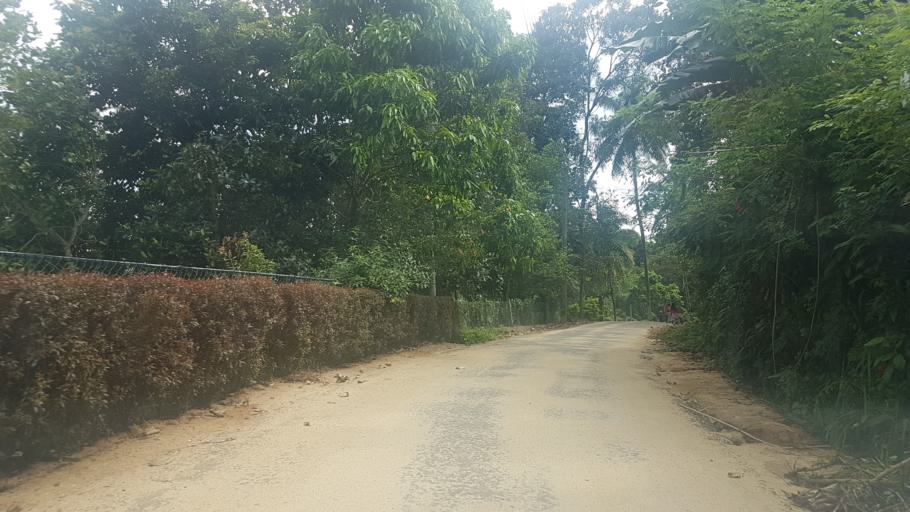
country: LK
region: Central
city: Gampola
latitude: 7.2220
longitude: 80.5852
